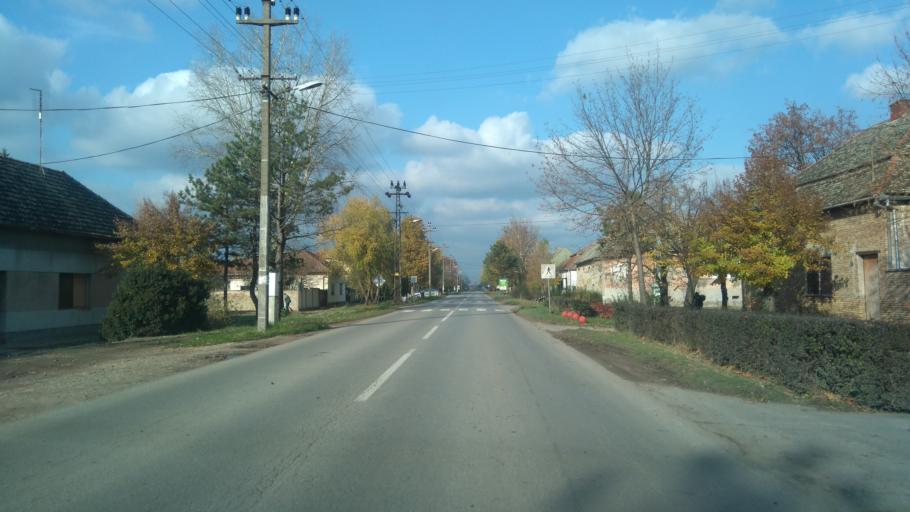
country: RS
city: Mol
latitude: 45.7659
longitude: 20.1293
